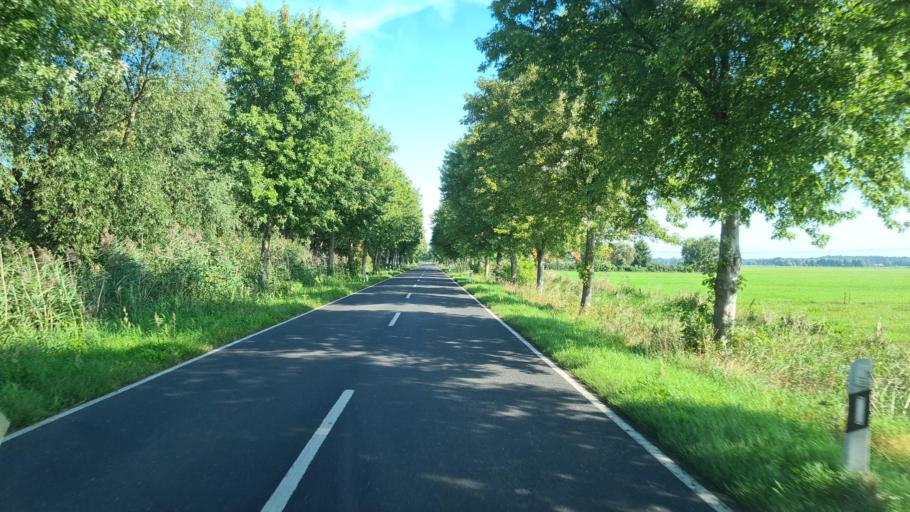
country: DE
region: Brandenburg
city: Friesack
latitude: 52.7648
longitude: 12.5902
